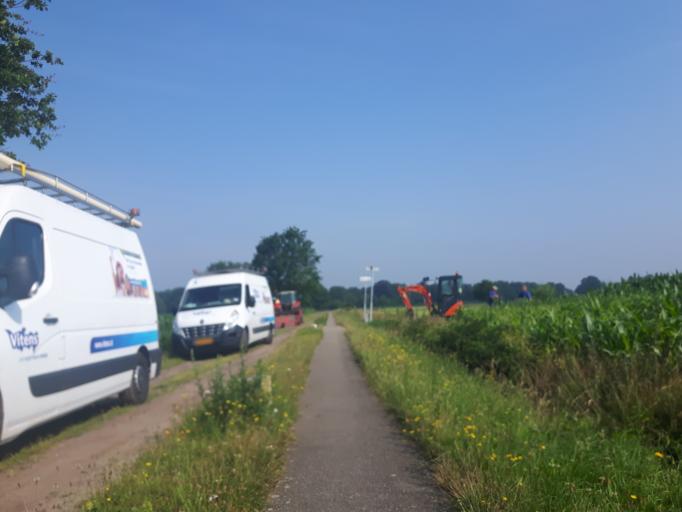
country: NL
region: Overijssel
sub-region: Gemeente Haaksbergen
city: Haaksbergen
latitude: 52.1888
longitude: 6.7893
